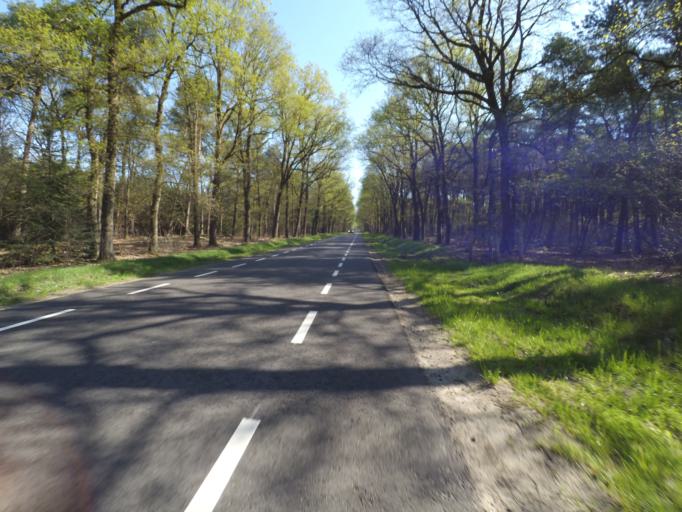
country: NL
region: Gelderland
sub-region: Gemeente Barneveld
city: Stroe
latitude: 52.1624
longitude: 5.7198
